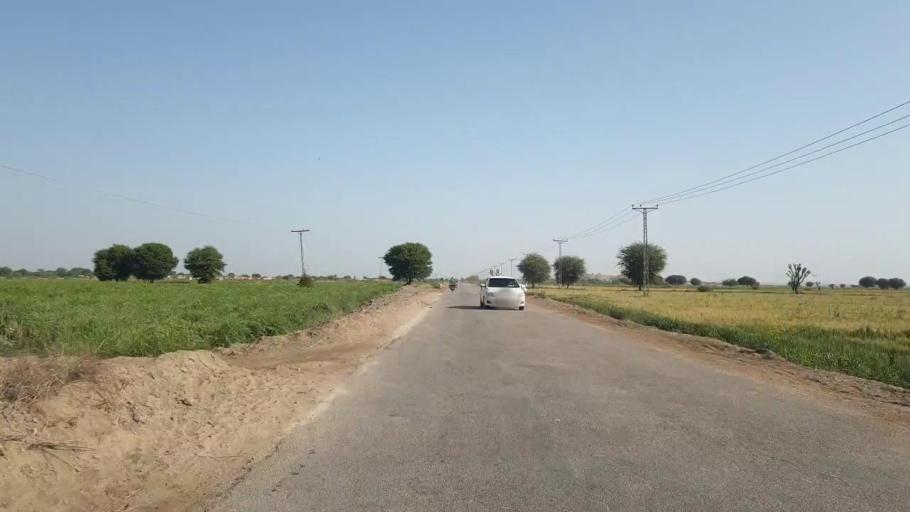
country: PK
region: Sindh
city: Umarkot
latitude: 25.4171
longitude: 69.7331
